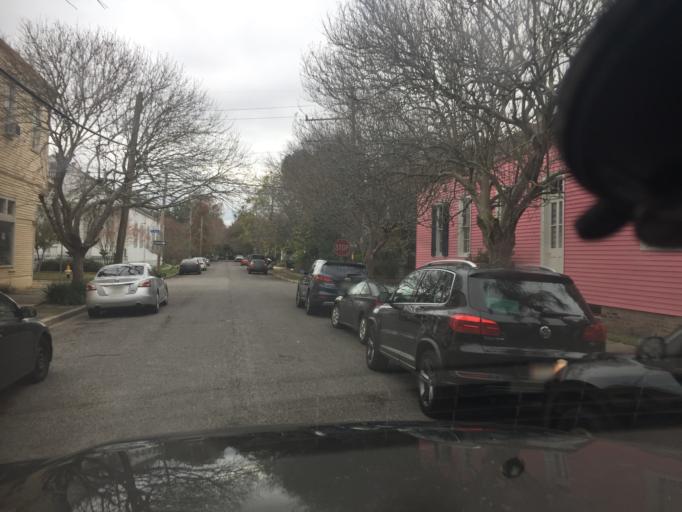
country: US
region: Louisiana
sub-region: Orleans Parish
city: New Orleans
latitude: 29.9768
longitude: -90.0817
